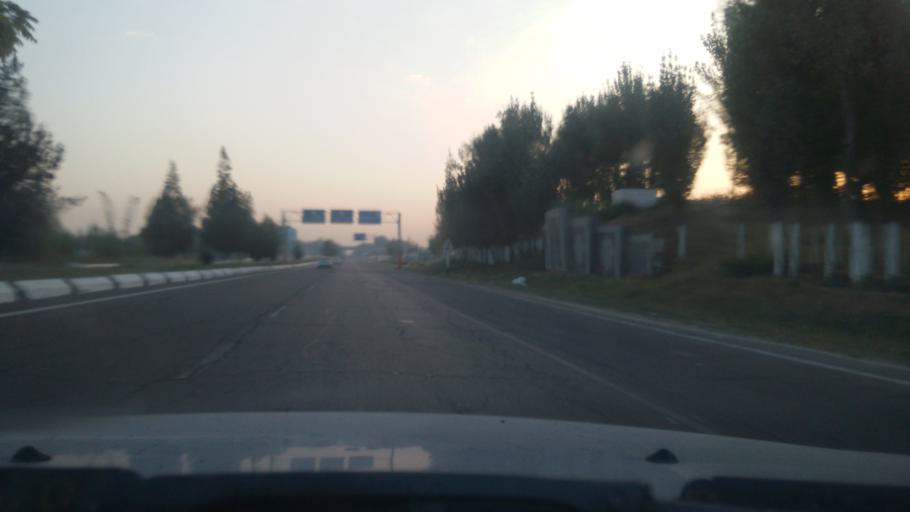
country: UZ
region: Toshkent
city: Amir Timur
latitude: 41.0490
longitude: 68.8934
